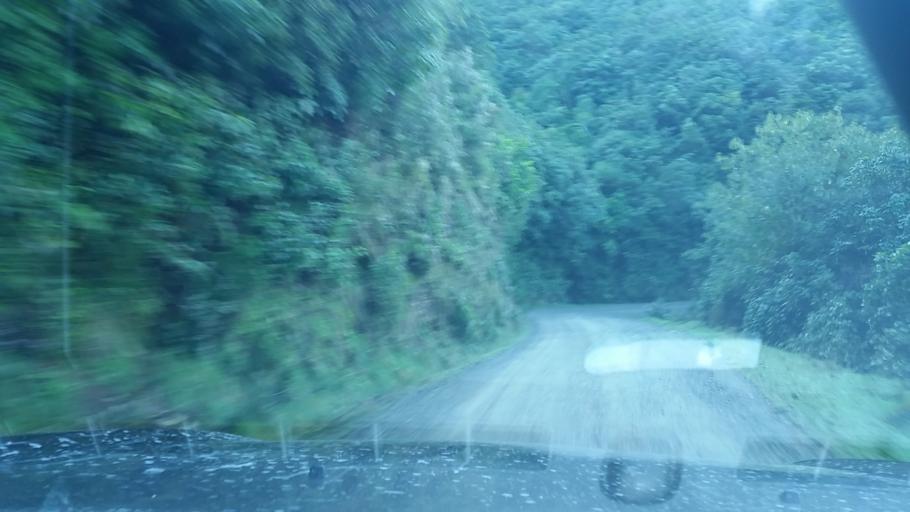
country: NZ
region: Marlborough
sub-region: Marlborough District
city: Picton
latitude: -41.1404
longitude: 174.0471
